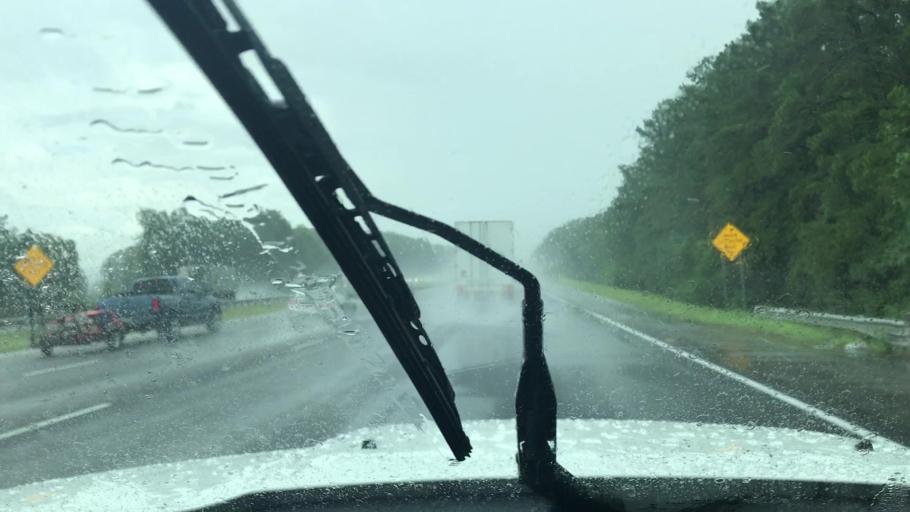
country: US
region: Georgia
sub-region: Chatham County
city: Port Wentworth
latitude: 32.1968
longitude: -81.1898
